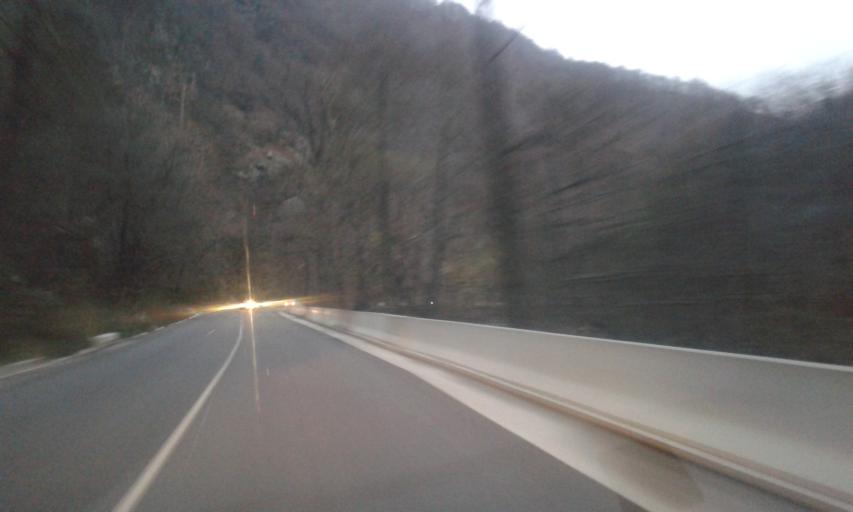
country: RO
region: Gorj
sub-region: Comuna Bumbesti-Jiu
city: Bumbesti-Jiu
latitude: 45.2041
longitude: 23.3761
